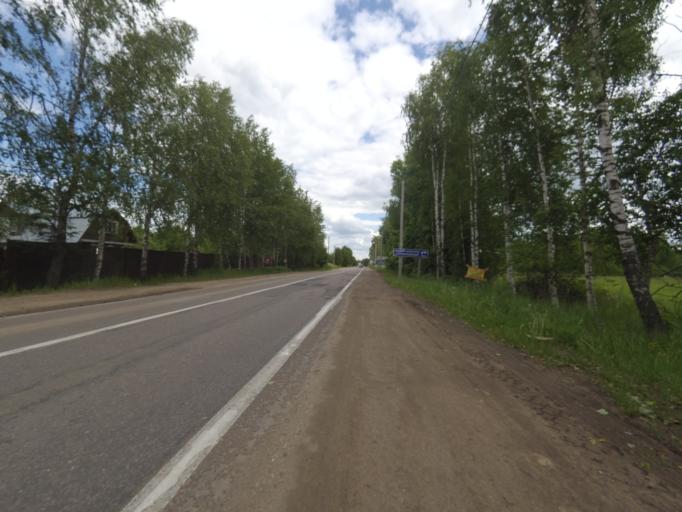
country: RU
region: Moskovskaya
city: Marfino
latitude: 56.0496
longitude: 37.5696
